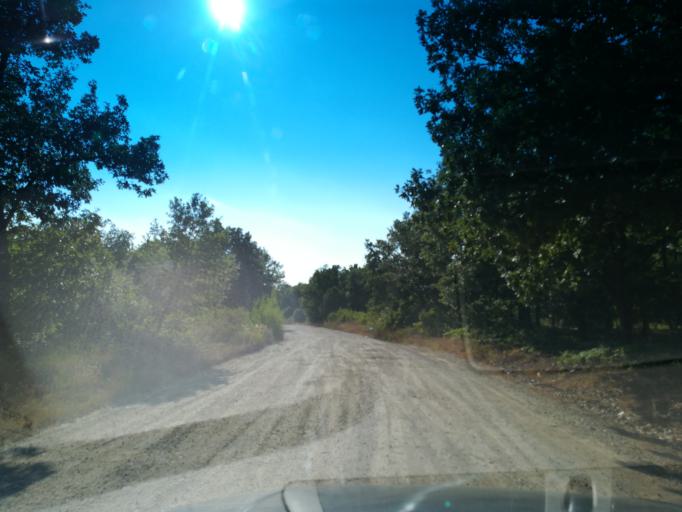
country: BG
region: Khaskovo
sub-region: Obshtina Mineralni Bani
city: Mineralni Bani
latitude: 41.9718
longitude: 25.3309
